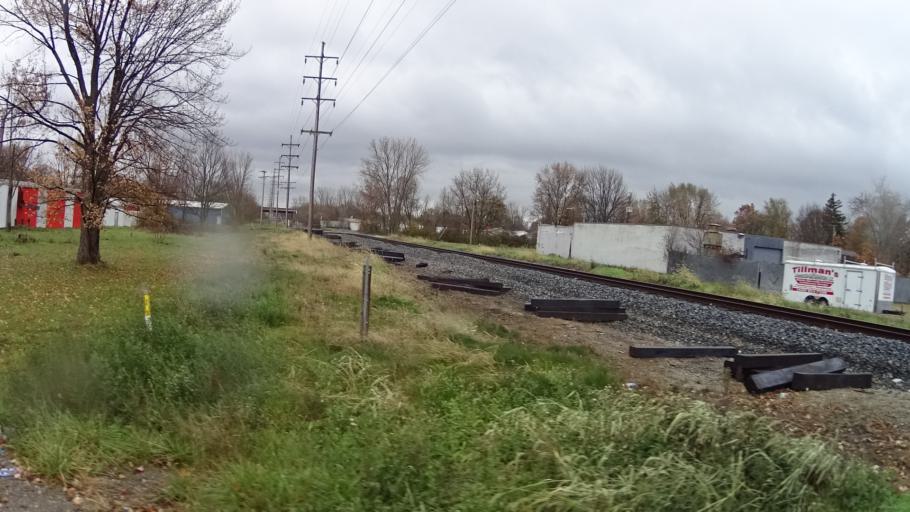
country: US
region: Ohio
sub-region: Lorain County
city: Elyria
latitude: 41.3891
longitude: -82.1246
